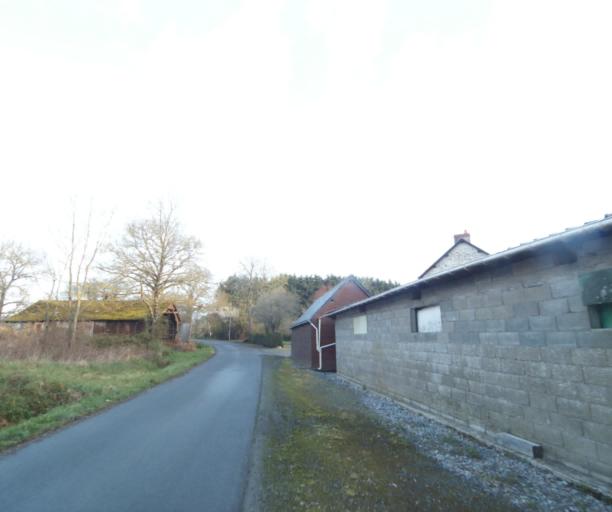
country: FR
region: Pays de la Loire
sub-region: Departement de la Loire-Atlantique
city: Savenay
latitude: 47.3947
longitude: -1.9140
